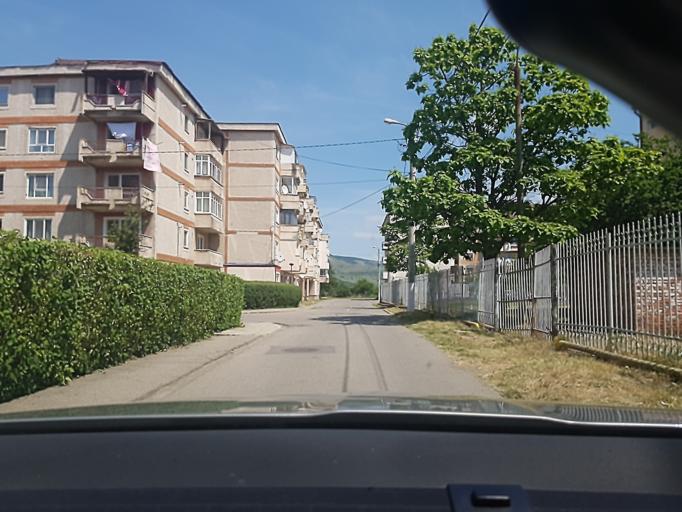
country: RO
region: Hunedoara
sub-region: Comuna Calan
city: Calan
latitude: 45.7322
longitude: 23.0283
